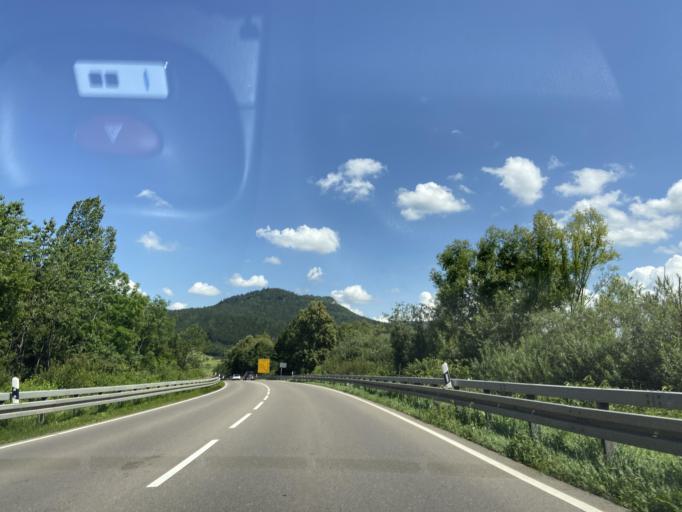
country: DE
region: Baden-Wuerttemberg
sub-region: Tuebingen Region
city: Balingen
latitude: 48.2335
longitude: 8.8867
